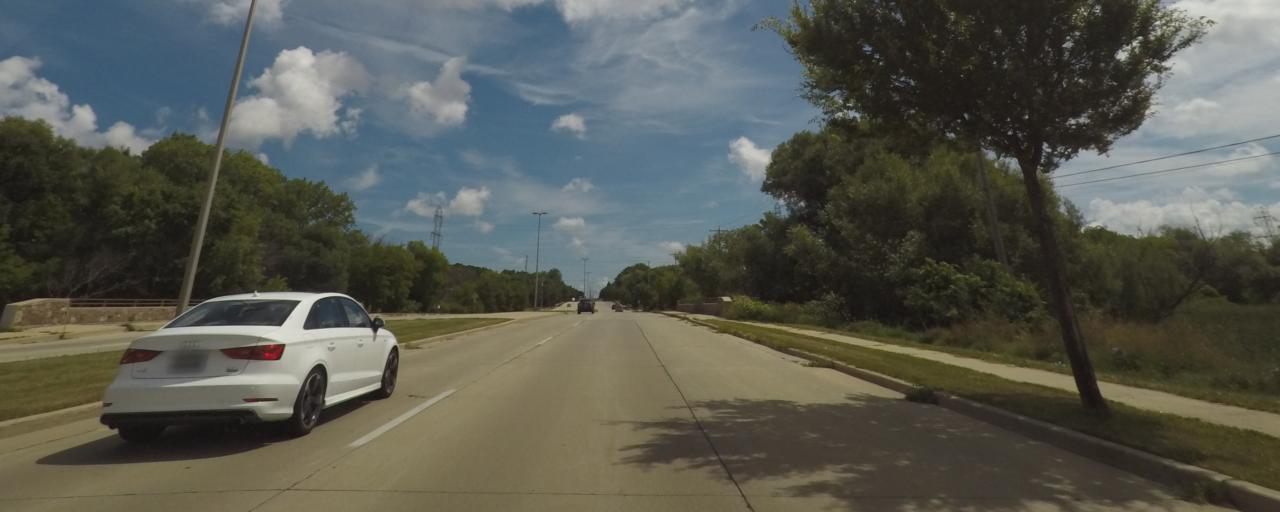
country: US
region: Wisconsin
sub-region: Milwaukee County
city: Hales Corners
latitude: 42.9592
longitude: -88.0408
